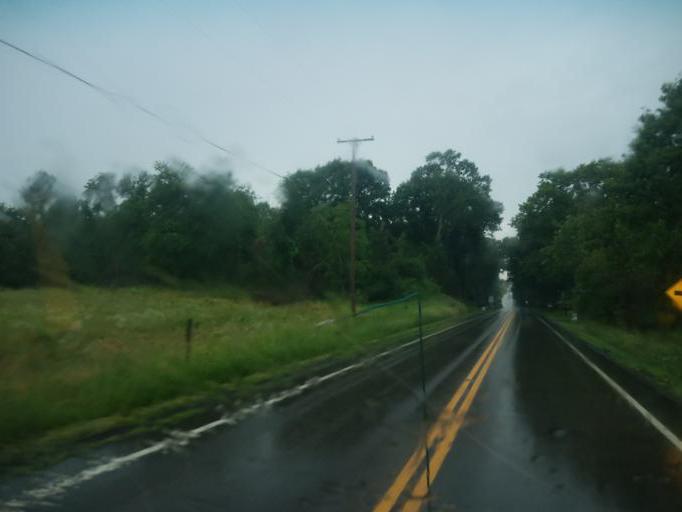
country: US
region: Ohio
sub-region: Stark County
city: Brewster
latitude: 40.7423
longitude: -81.6324
